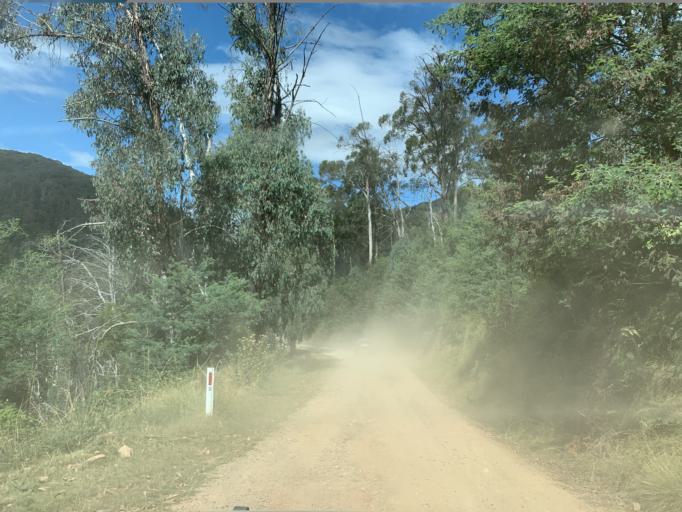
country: AU
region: Victoria
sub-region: Mansfield
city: Mansfield
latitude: -37.0985
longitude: 146.4987
